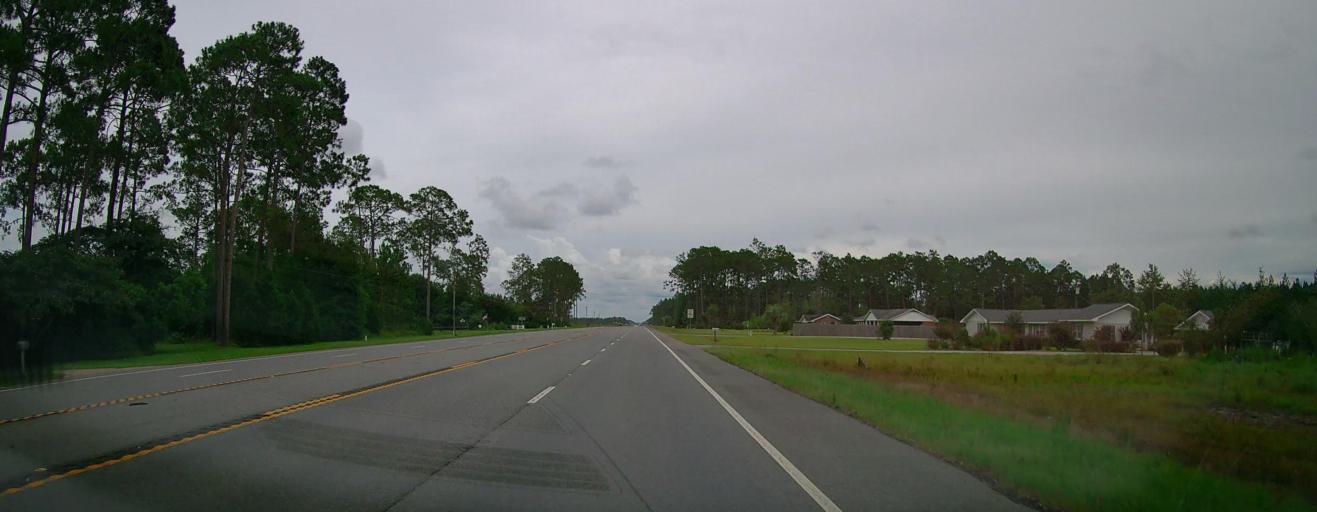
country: US
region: Georgia
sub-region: Appling County
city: Baxley
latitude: 31.7623
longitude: -82.3020
